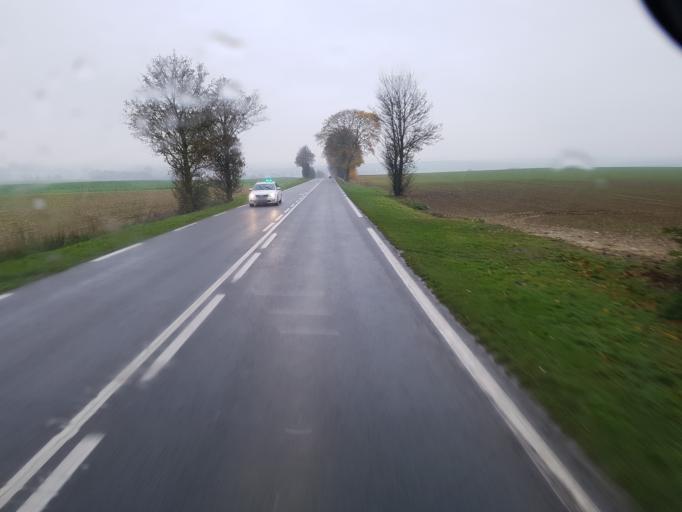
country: FR
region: Picardie
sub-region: Departement de l'Aisne
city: Omissy
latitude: 49.9071
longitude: 3.2591
